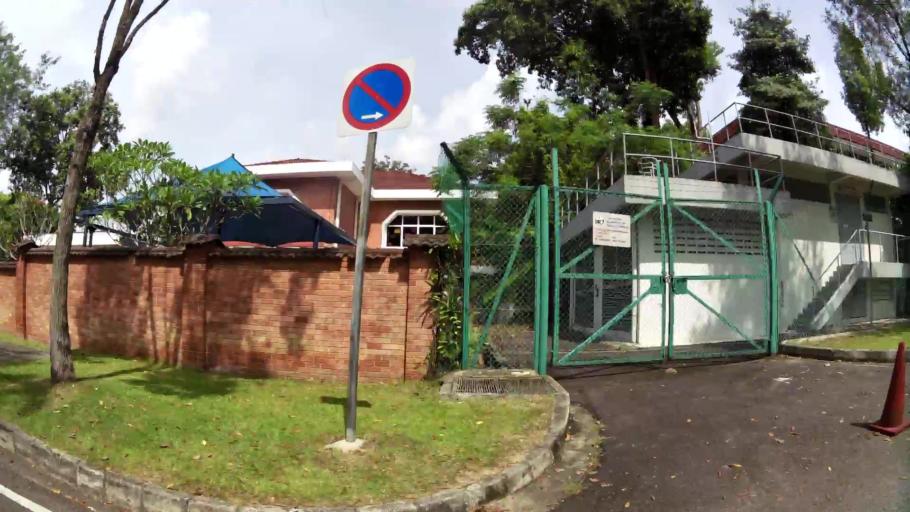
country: SG
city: Singapore
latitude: 1.3454
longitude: 103.7902
